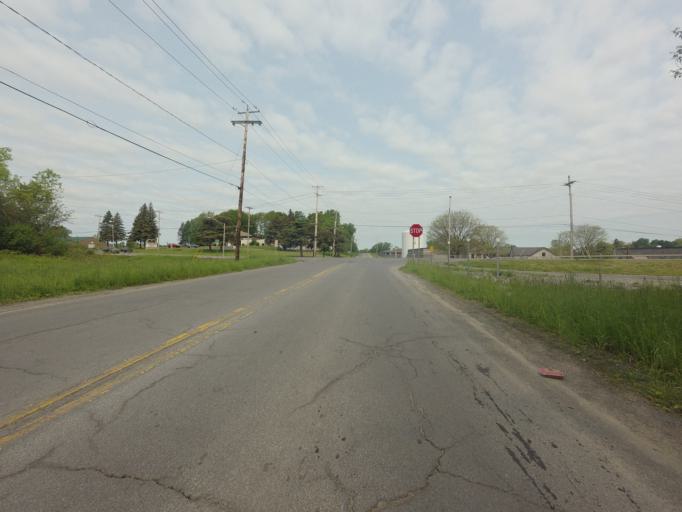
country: US
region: New York
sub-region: Jefferson County
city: Watertown
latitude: 43.9747
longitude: -75.8748
